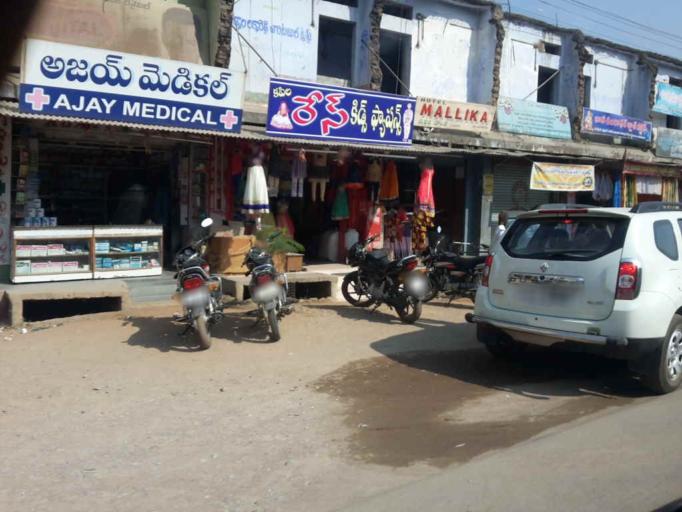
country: IN
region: Telangana
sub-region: Karimnagar
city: Koratla
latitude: 18.8473
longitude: 78.6252
